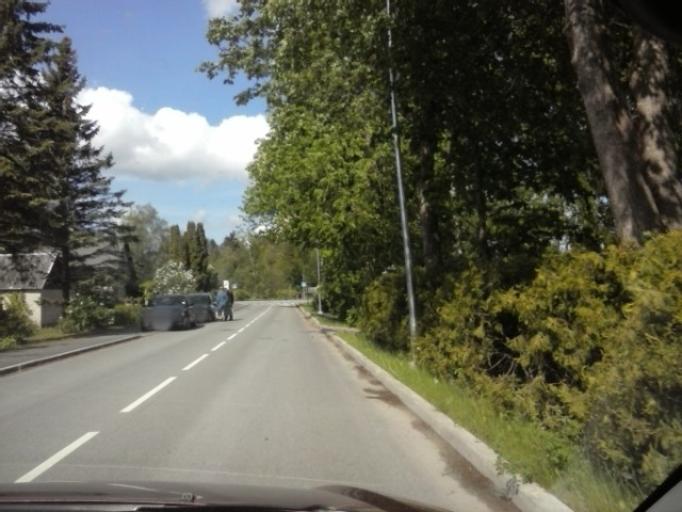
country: EE
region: Raplamaa
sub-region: Rapla vald
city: Rapla
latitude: 58.9923
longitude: 24.8255
